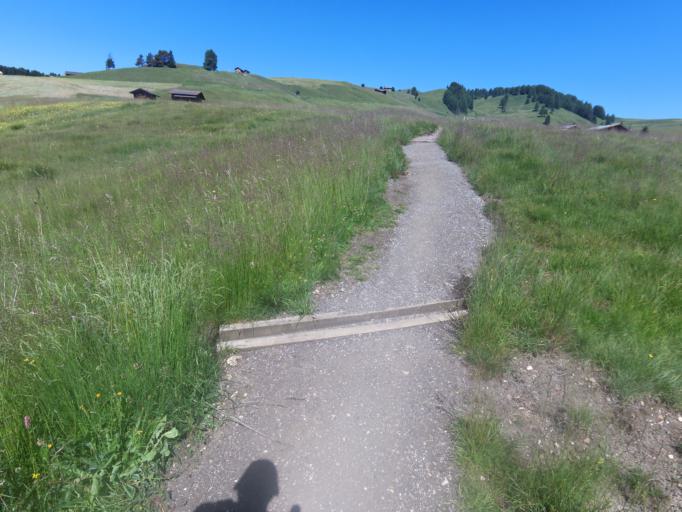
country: IT
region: Trentino-Alto Adige
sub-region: Bolzano
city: Ortisei
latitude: 46.5333
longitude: 11.6692
